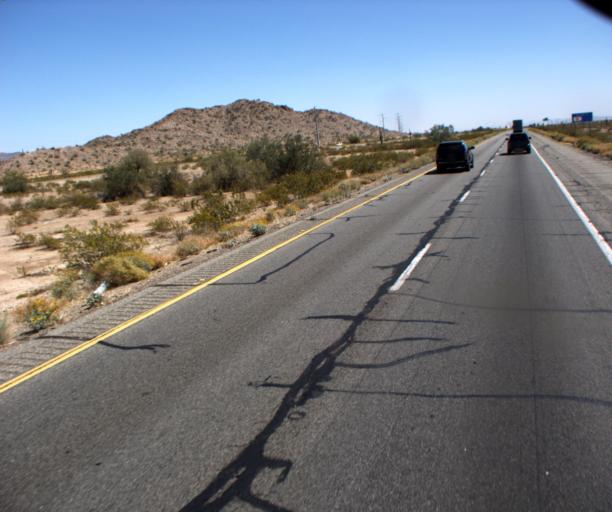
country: US
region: Arizona
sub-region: Maricopa County
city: Buckeye
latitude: 33.4305
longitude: -112.6412
